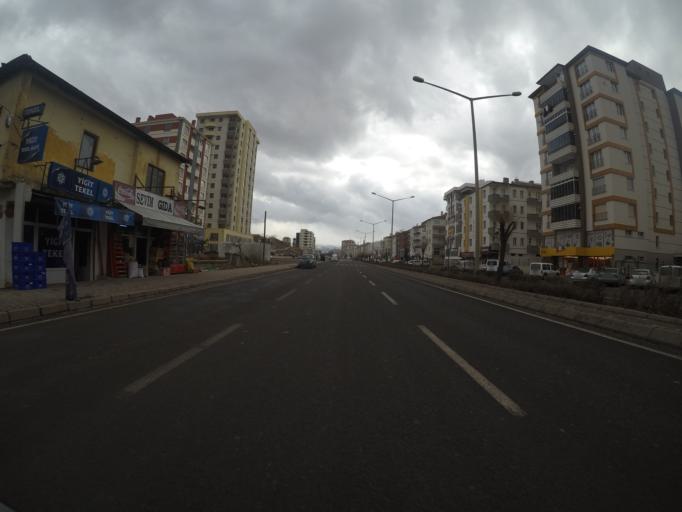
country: TR
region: Kayseri
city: Melikgazi
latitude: 38.7577
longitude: 35.4671
